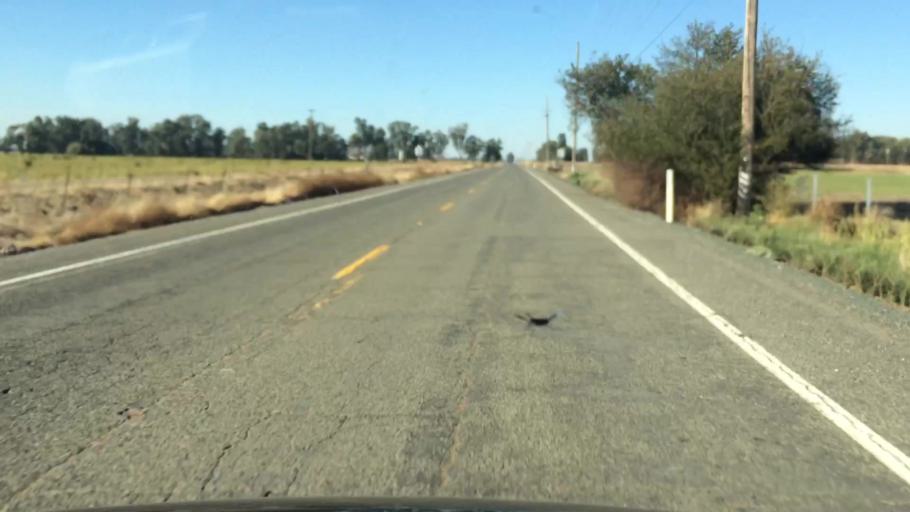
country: US
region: California
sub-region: Sacramento County
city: Clay
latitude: 38.3490
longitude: -121.1683
